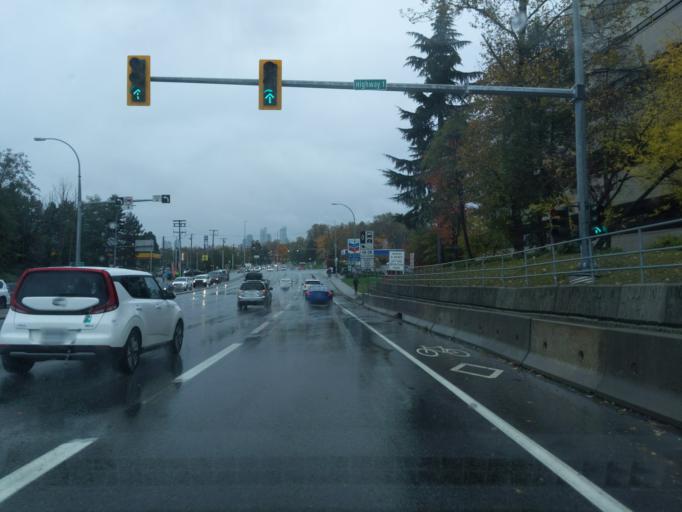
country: CA
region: British Columbia
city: Burnaby
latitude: 49.2561
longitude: -123.0044
